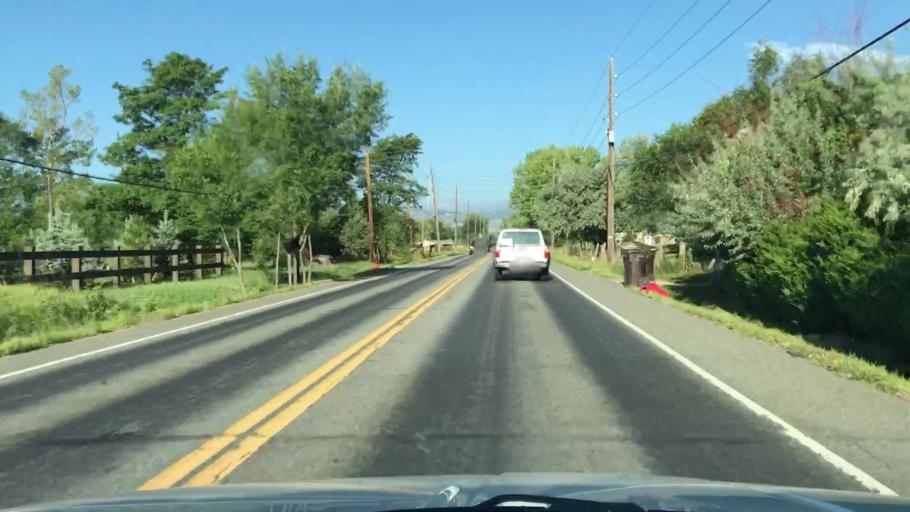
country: US
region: Colorado
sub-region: Boulder County
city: Gunbarrel
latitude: 40.0510
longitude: -105.1968
